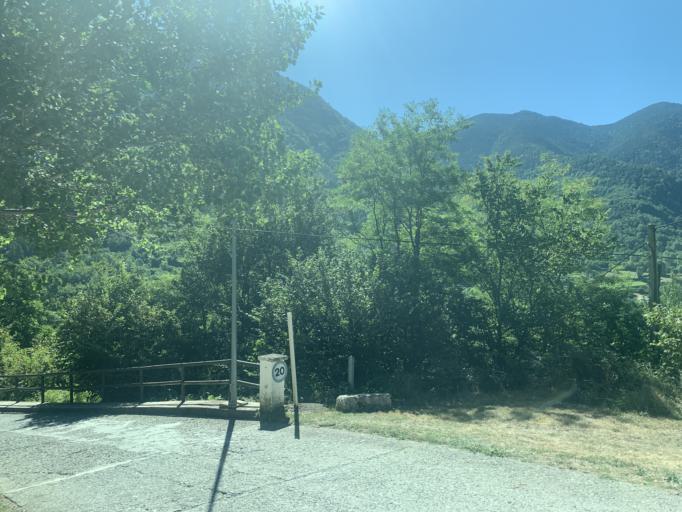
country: ES
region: Aragon
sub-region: Provincia de Huesca
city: Broto
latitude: 42.6380
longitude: -0.1104
